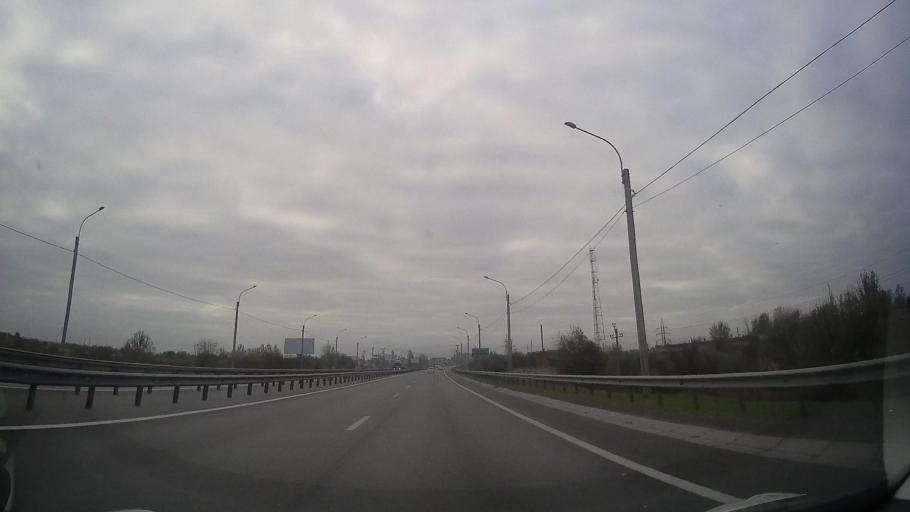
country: RU
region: Rostov
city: Bataysk
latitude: 47.1601
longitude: 39.7644
